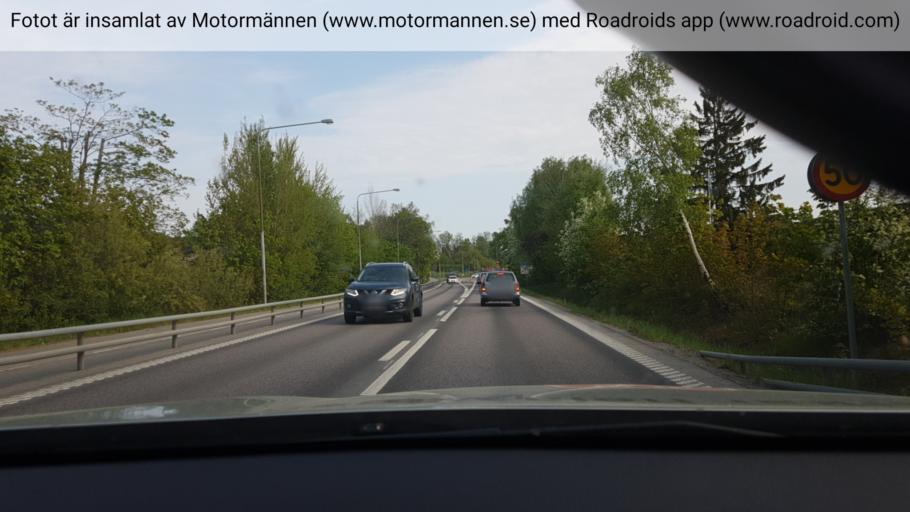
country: SE
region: Stockholm
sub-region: Tyreso Kommun
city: Bollmora
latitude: 59.2152
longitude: 18.2020
